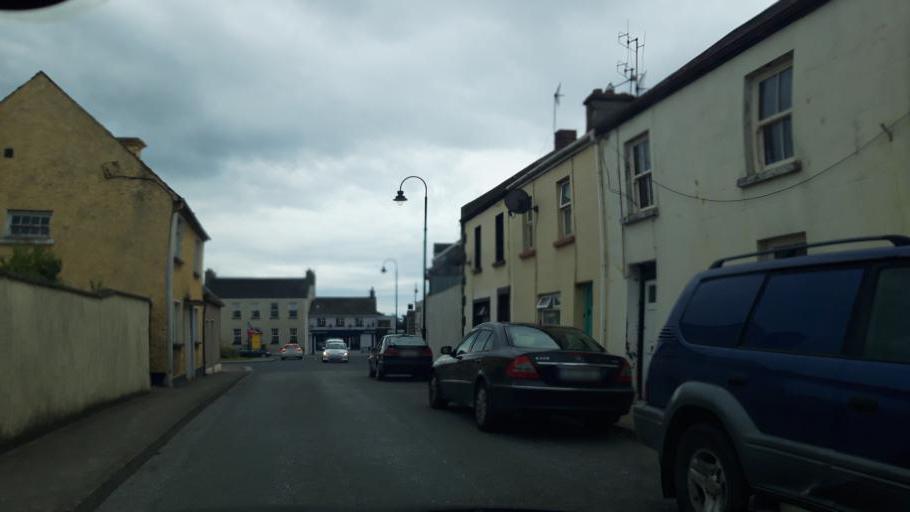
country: IE
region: Leinster
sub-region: Kilkenny
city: Ballyragget
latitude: 52.7892
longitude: -7.3351
